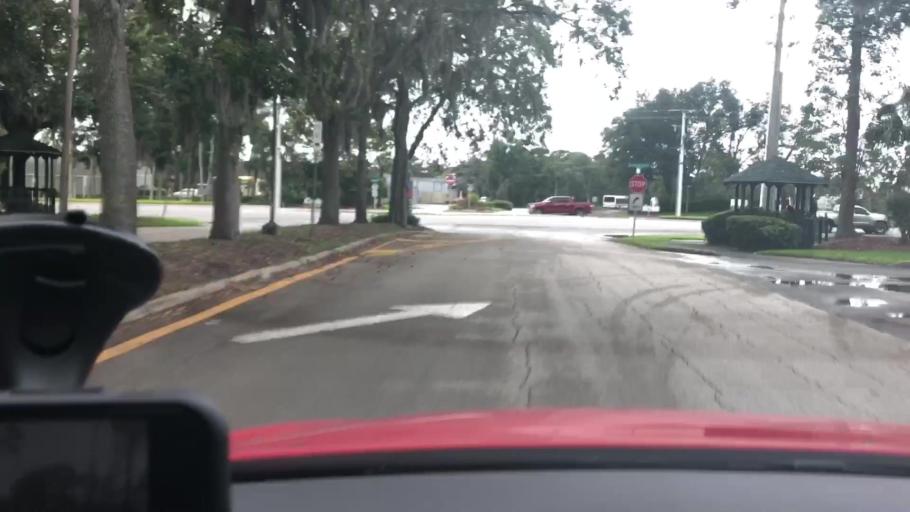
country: US
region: Florida
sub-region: Volusia County
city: Port Orange
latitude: 29.1268
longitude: -81.0078
